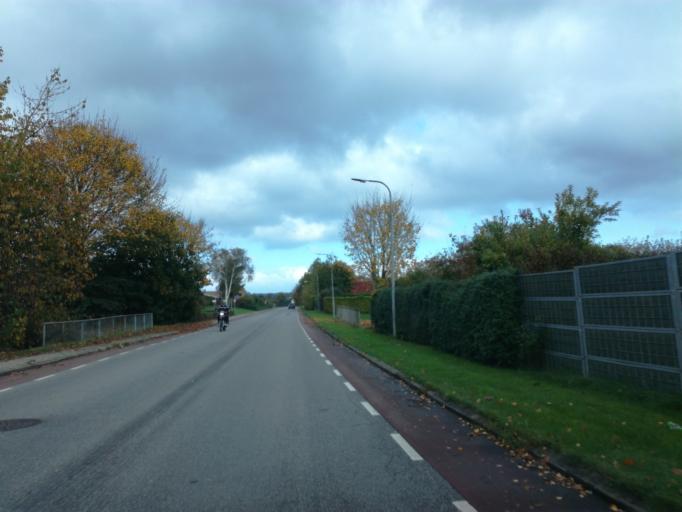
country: DK
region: South Denmark
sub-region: Vejle Kommune
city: Borkop
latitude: 55.6376
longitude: 9.6528
